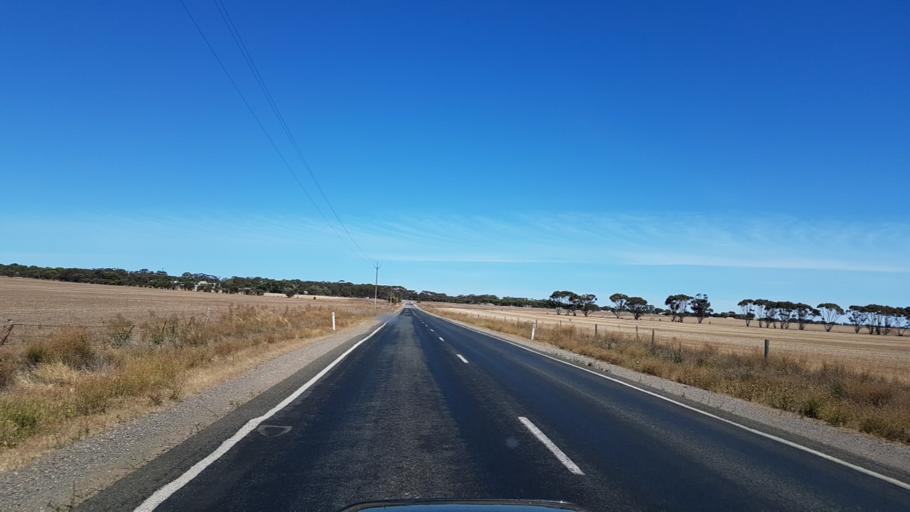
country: AU
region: South Australia
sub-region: Yorke Peninsula
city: Maitland
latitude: -34.3590
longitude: 137.6659
